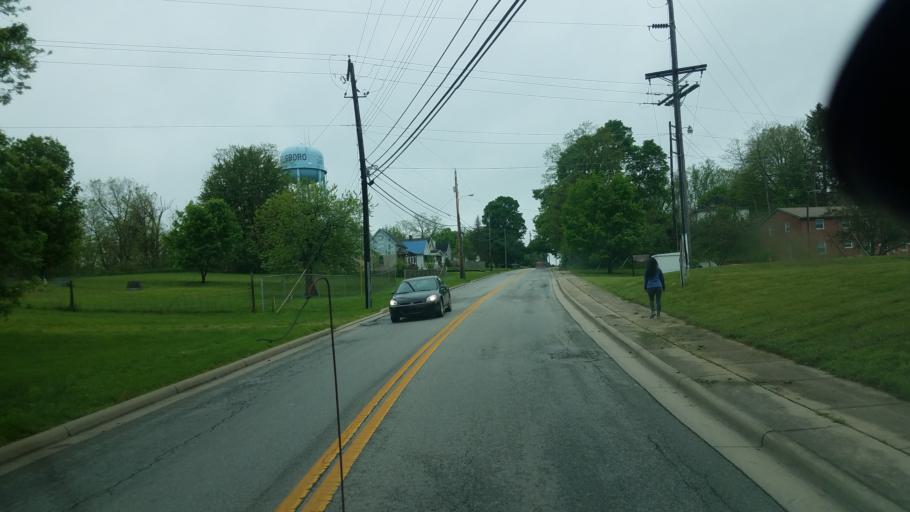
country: US
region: Ohio
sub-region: Highland County
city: Hillsboro
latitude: 39.2125
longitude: -83.6118
